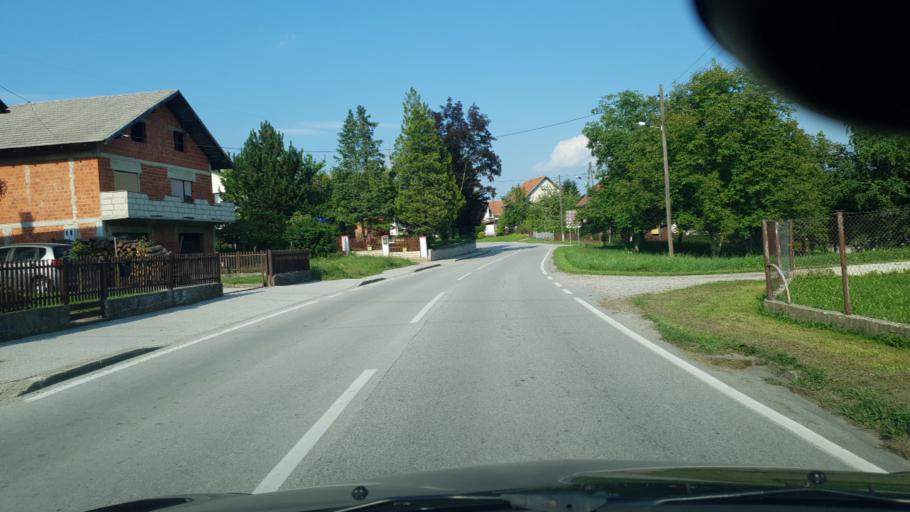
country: HR
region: Krapinsko-Zagorska
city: Oroslavje
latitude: 45.9726
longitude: 15.9175
